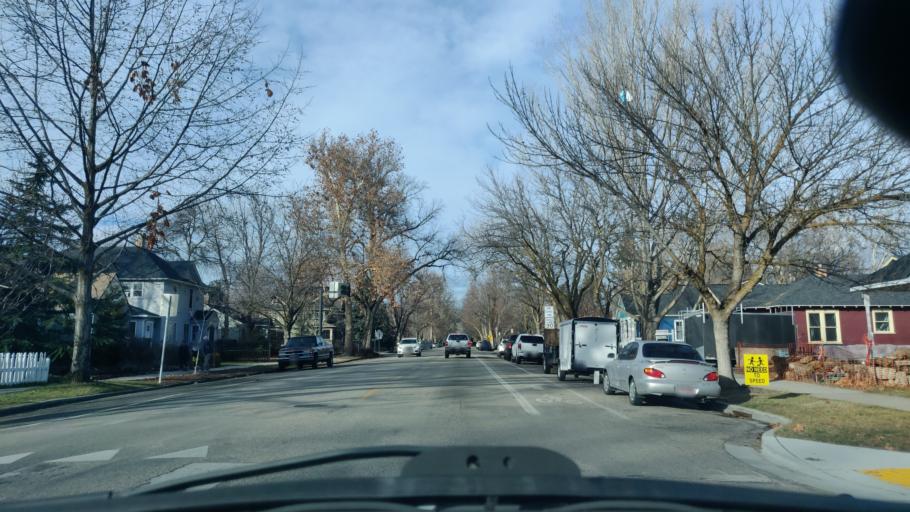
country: US
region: Idaho
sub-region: Ada County
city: Boise
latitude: 43.6266
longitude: -116.2058
